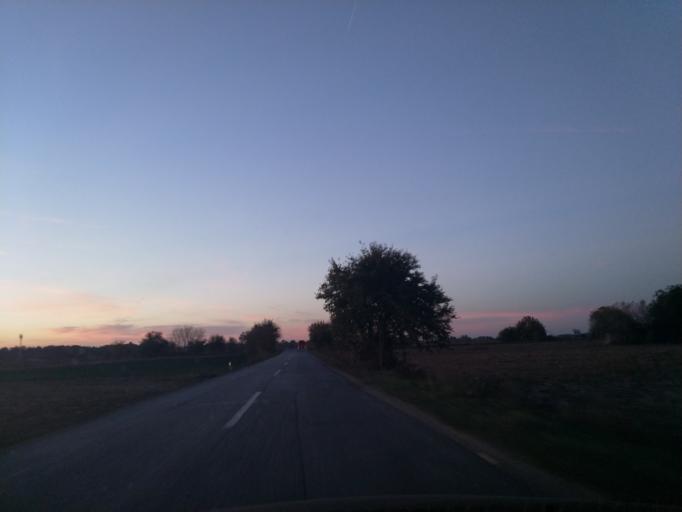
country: RS
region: Central Serbia
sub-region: Pomoravski Okrug
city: Svilajnac
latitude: 44.2304
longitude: 21.1434
